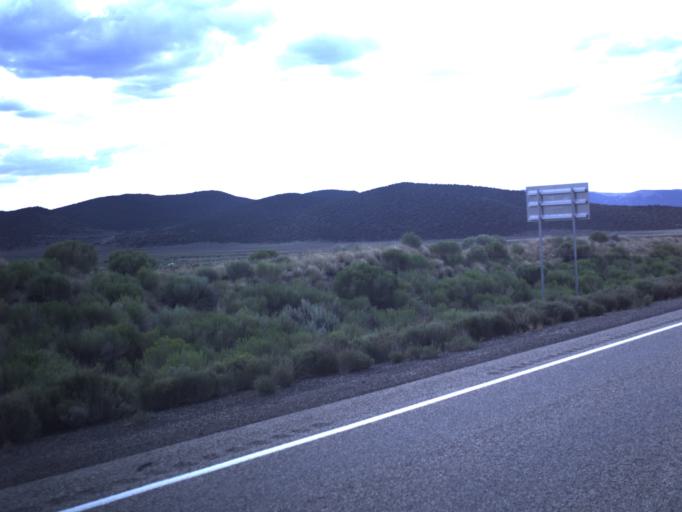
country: US
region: Utah
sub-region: Beaver County
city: Beaver
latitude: 38.0485
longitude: -112.5735
